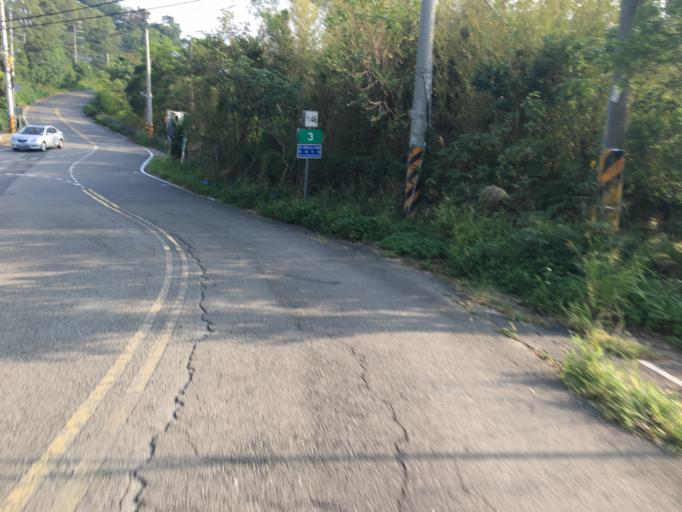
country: TW
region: Taiwan
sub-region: Hsinchu
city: Hsinchu
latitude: 24.7435
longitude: 121.0378
